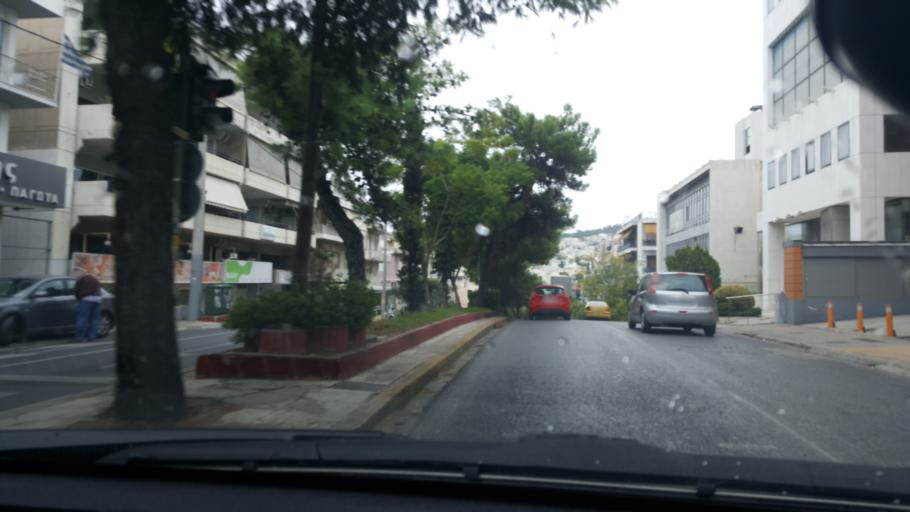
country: GR
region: Attica
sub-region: Nomarchia Athinas
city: Neo Psychiko
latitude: 37.9960
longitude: 23.7721
